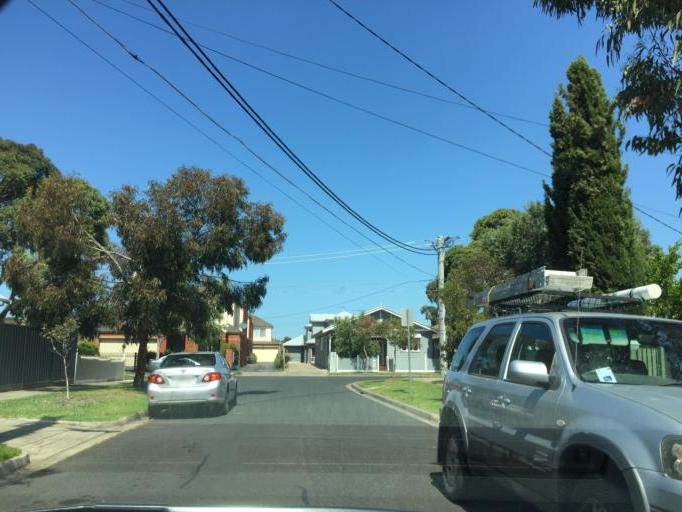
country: AU
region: Victoria
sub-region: Maribyrnong
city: Maidstone
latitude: -37.7890
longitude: 144.8729
